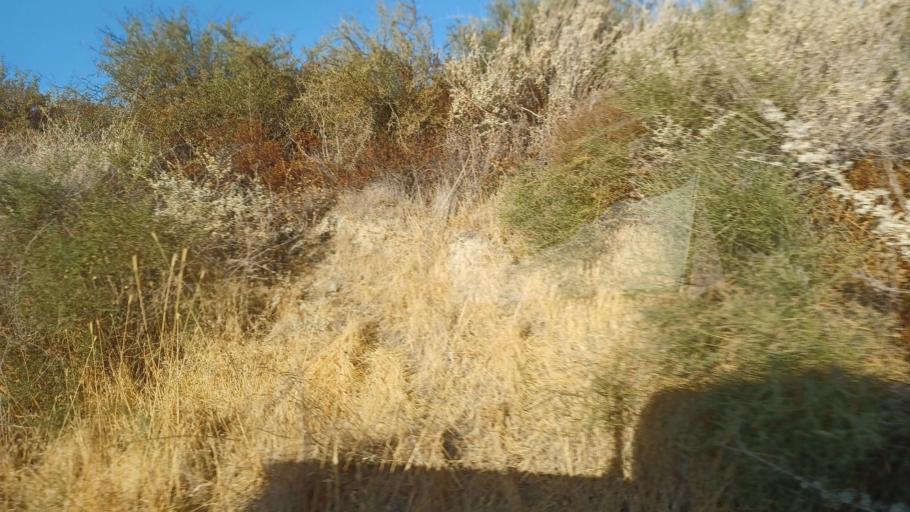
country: CY
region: Pafos
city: Polis
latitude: 34.9972
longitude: 32.4672
